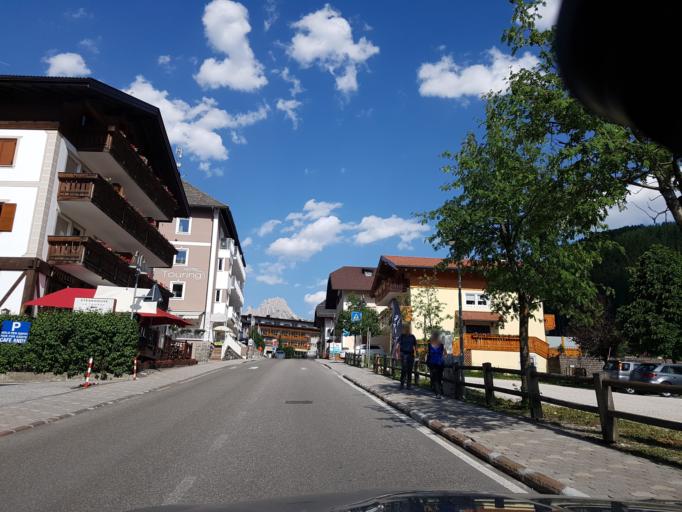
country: IT
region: Trentino-Alto Adige
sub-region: Bolzano
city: Santa Cristina Valgardena
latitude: 46.5580
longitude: 11.7235
